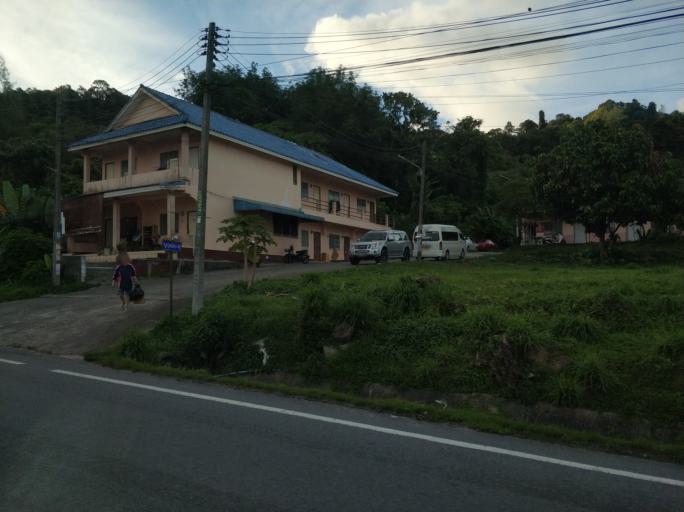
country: TH
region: Phuket
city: Kathu
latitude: 7.9048
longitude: 98.3260
